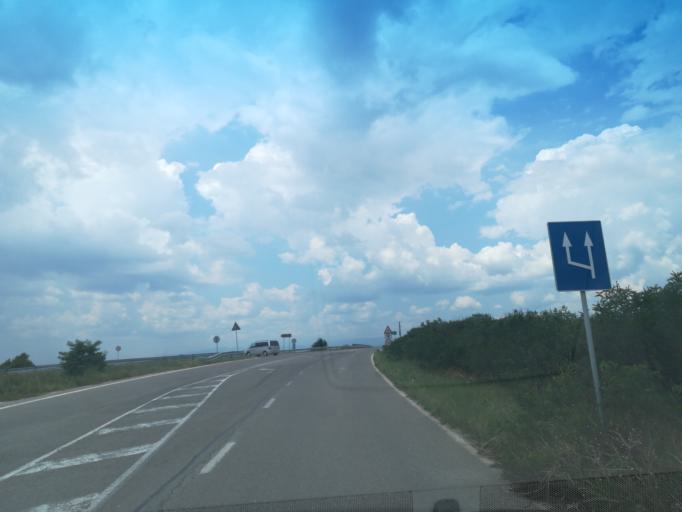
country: BG
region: Stara Zagora
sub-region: Obshtina Chirpan
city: Chirpan
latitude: 42.1909
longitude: 25.1966
